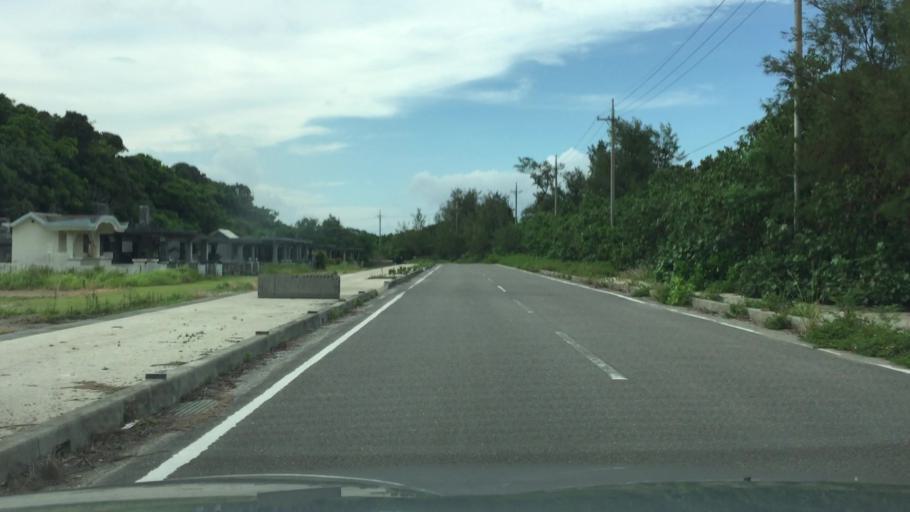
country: JP
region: Okinawa
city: Ishigaki
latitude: 24.4645
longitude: 124.1423
